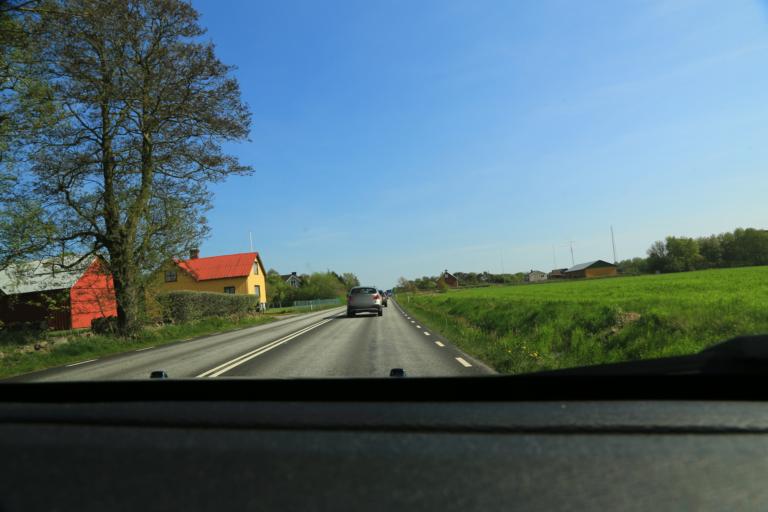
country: SE
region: Halland
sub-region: Varbergs Kommun
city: Varberg
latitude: 57.1608
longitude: 12.2434
